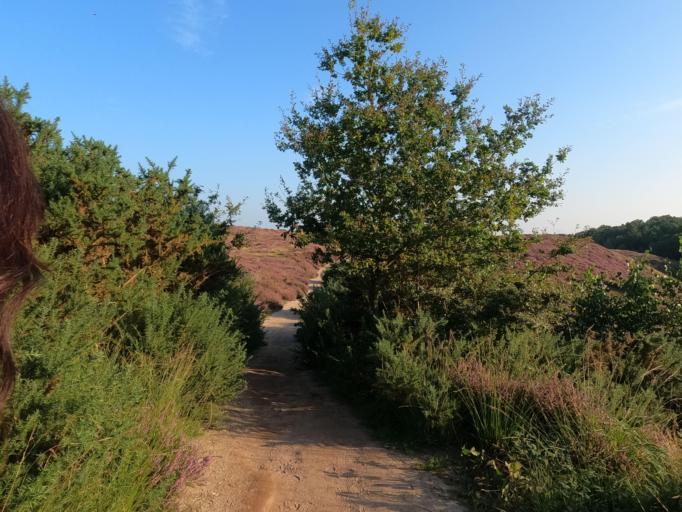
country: NL
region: Gelderland
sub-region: Gemeente Rheden
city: Rheden
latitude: 52.0247
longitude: 6.0270
